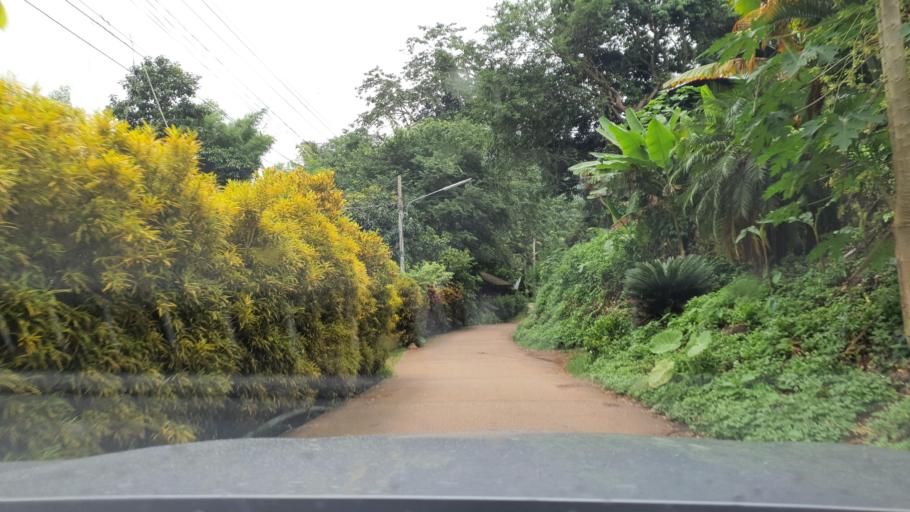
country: TH
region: Chiang Mai
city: Samoeng
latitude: 18.7981
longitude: 98.7935
